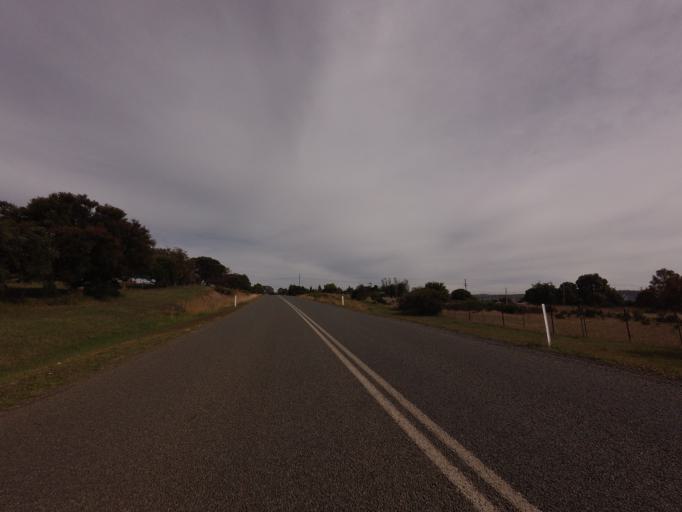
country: AU
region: Tasmania
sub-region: Brighton
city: Bridgewater
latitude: -42.3102
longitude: 147.3692
